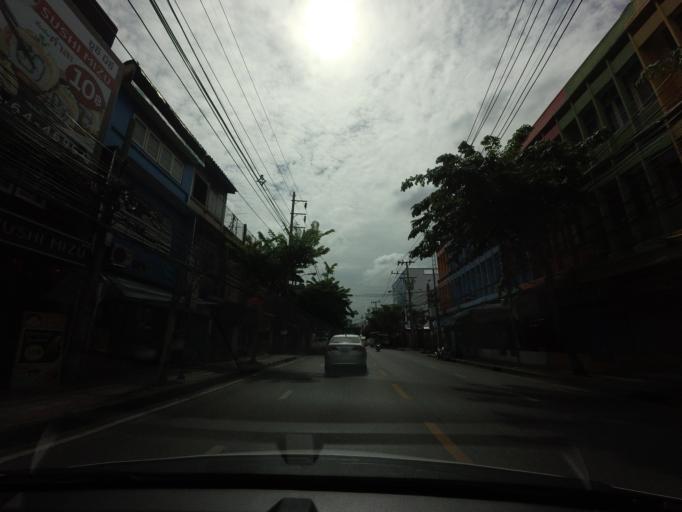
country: TH
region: Bangkok
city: Chom Thong
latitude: 13.6979
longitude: 100.4722
